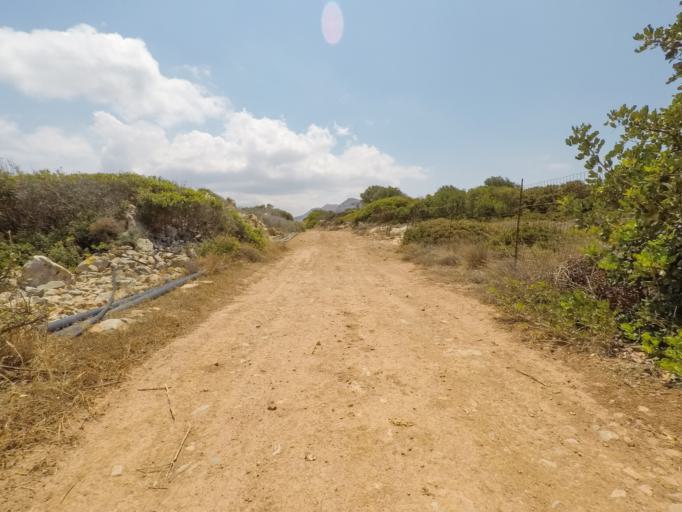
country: GR
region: Crete
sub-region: Nomos Lasithiou
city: Elounda
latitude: 35.3154
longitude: 25.7417
